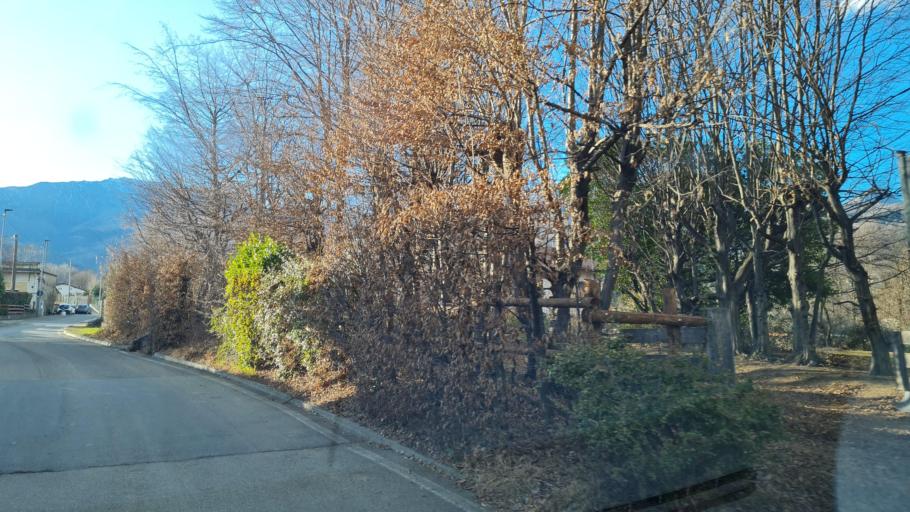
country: IT
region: Piedmont
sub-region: Provincia di Biella
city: Occhieppo Superiore
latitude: 45.5709
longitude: 8.0031
